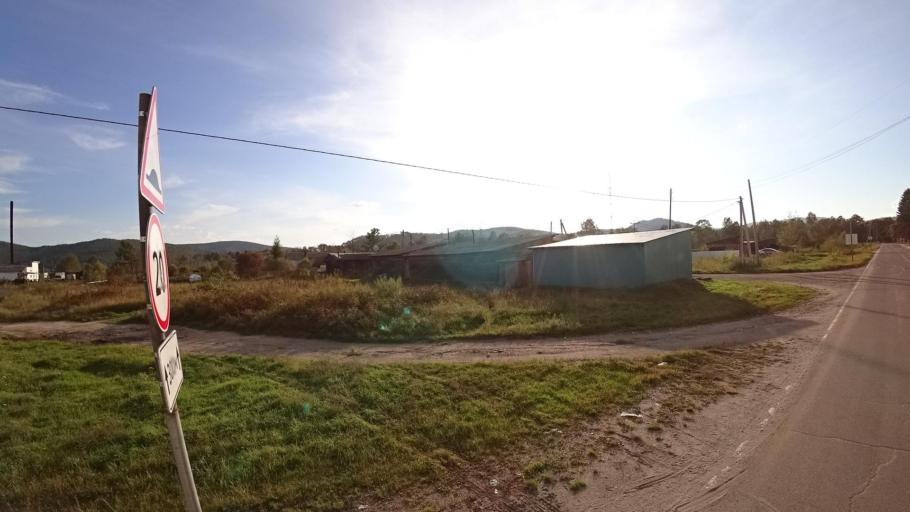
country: RU
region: Jewish Autonomous Oblast
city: Kul'dur
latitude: 49.2022
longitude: 131.6237
